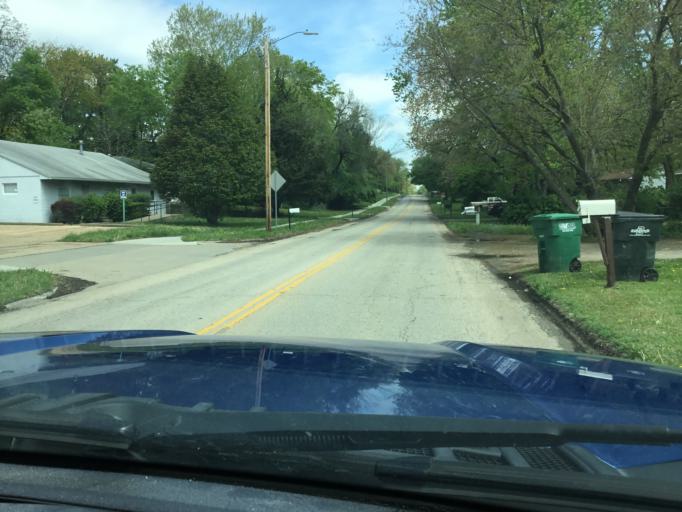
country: US
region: Kansas
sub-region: Shawnee County
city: Topeka
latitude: 39.0228
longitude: -95.6607
